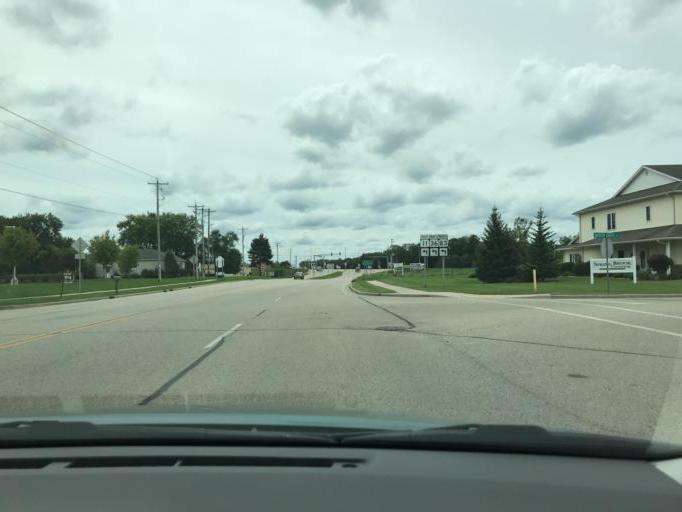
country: US
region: Wisconsin
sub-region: Racine County
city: Burlington
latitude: 42.6601
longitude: -88.2613
